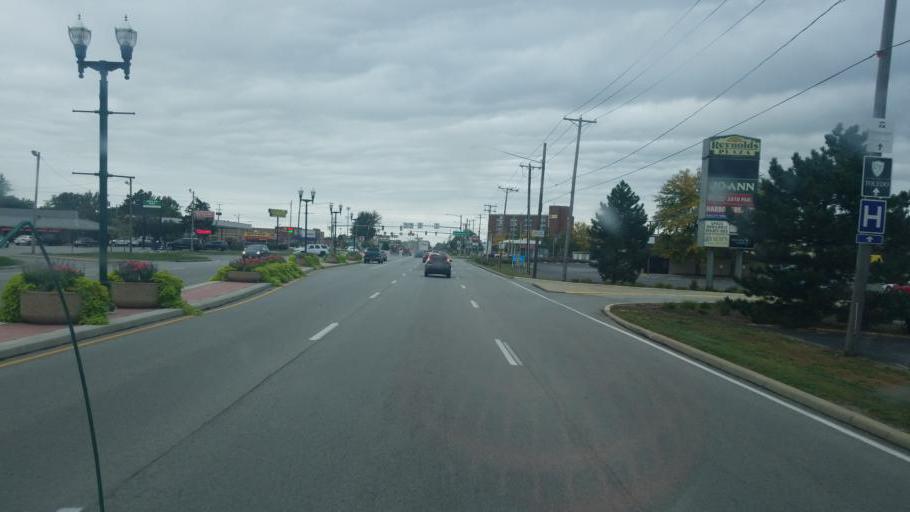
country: US
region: Ohio
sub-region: Lucas County
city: Maumee
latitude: 41.5928
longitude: -83.6646
